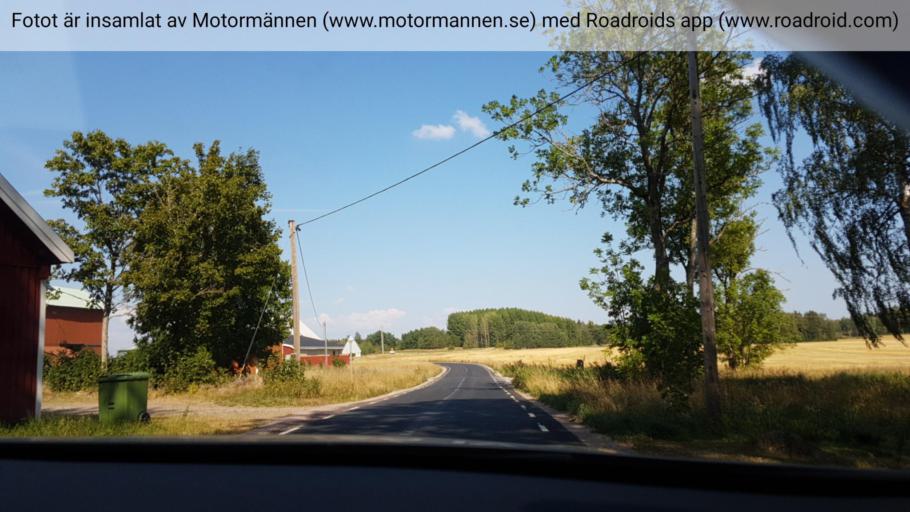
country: SE
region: Vaestra Goetaland
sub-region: Skovde Kommun
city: Stopen
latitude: 58.5845
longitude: 13.8584
